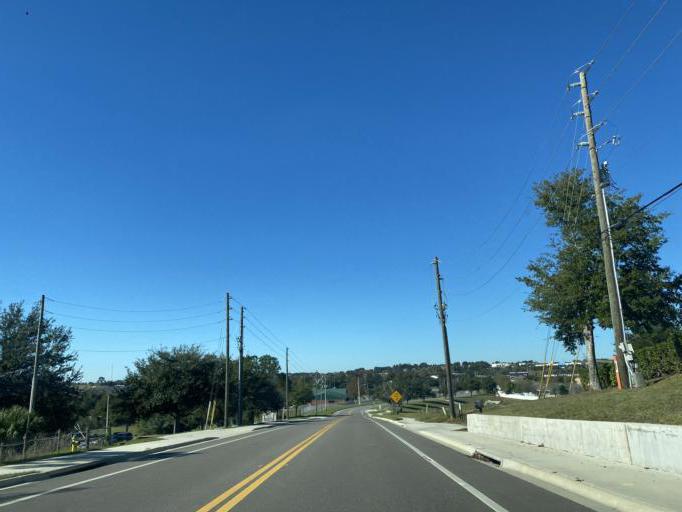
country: US
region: Florida
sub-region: Lake County
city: Minneola
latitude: 28.5251
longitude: -81.7178
